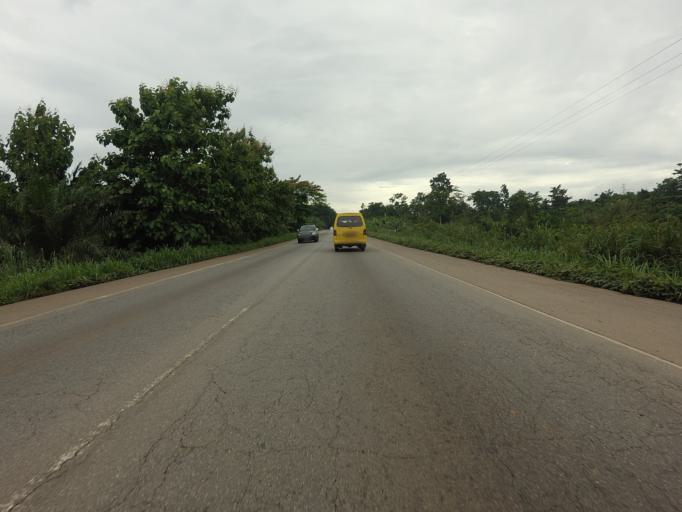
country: GH
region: Eastern
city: Nkawkaw
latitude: 6.4834
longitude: -0.6673
